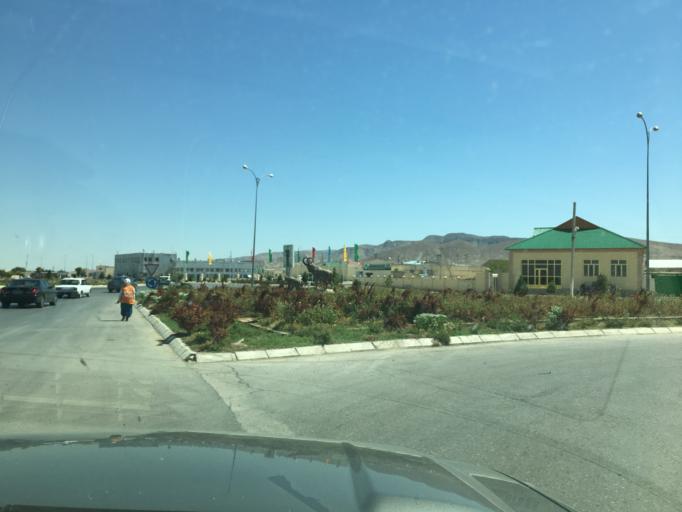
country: TM
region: Balkan
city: Serdar
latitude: 38.9812
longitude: 56.2964
